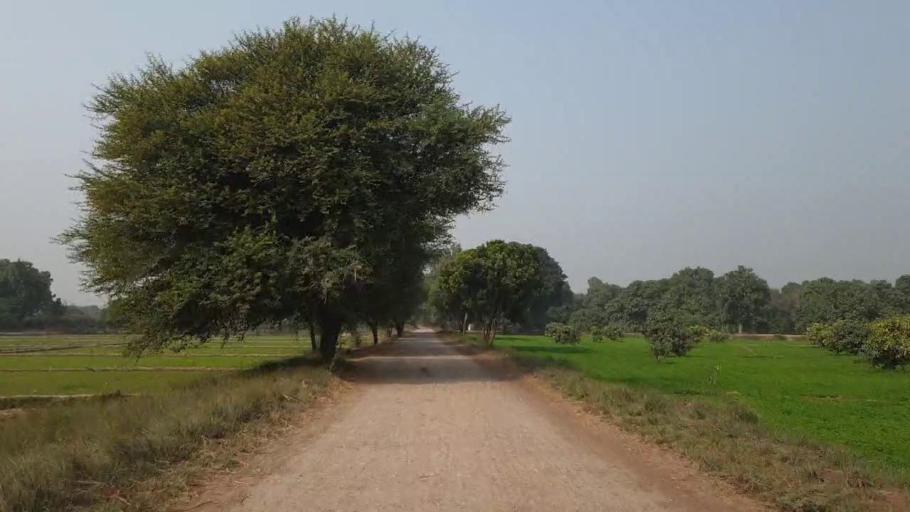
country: PK
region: Sindh
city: Tando Muhammad Khan
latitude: 25.2149
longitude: 68.5561
